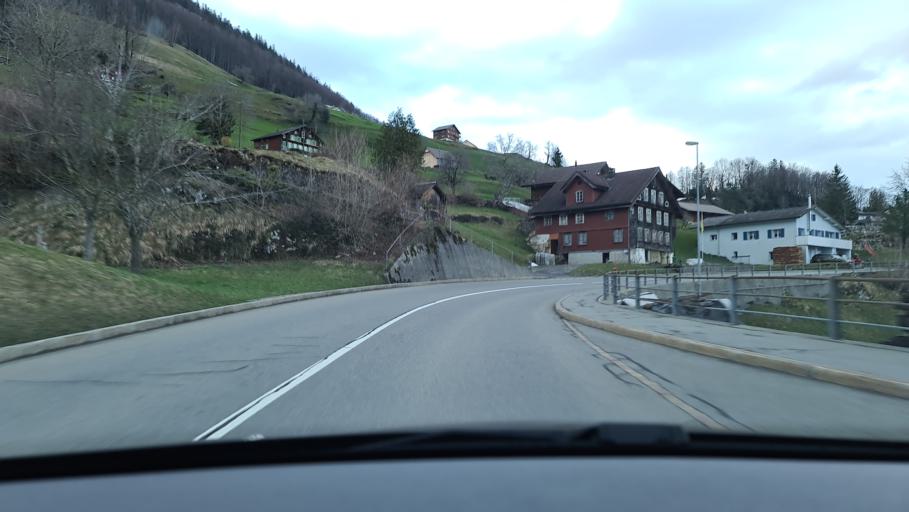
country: CH
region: Uri
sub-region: Uri
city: Bauen
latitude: 46.9653
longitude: 8.5795
